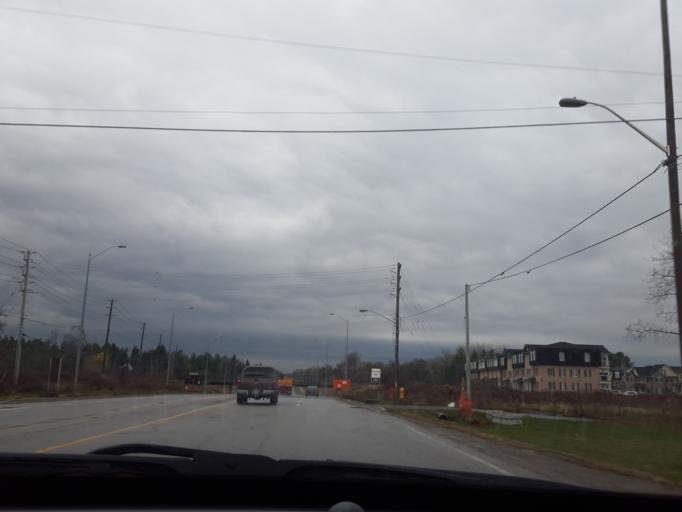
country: CA
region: Ontario
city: Pickering
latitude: 43.8803
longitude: -79.0880
